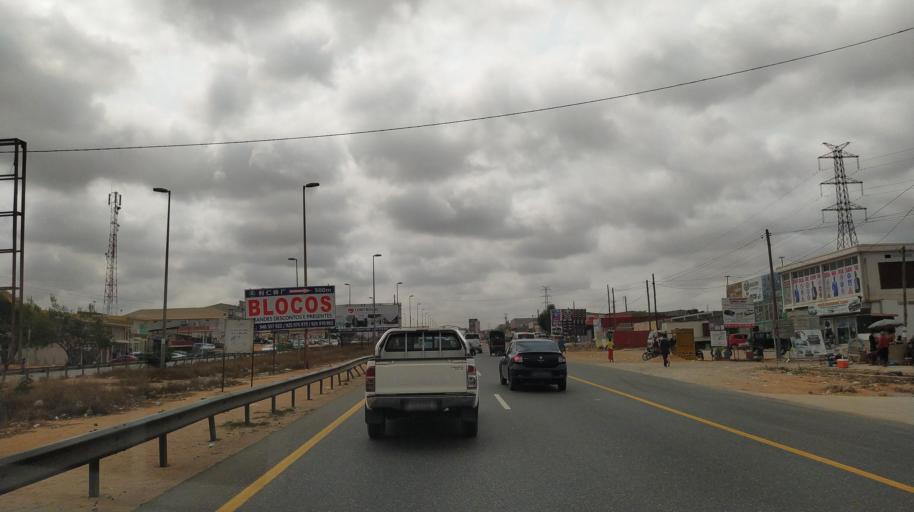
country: AO
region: Luanda
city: Luanda
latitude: -8.9731
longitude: 13.3013
